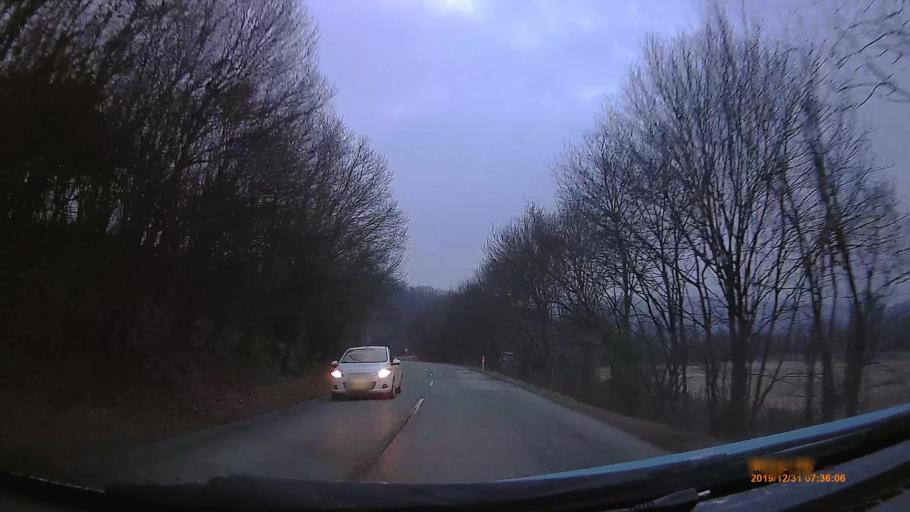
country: HU
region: Heves
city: Sirok
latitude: 47.9238
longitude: 20.1663
